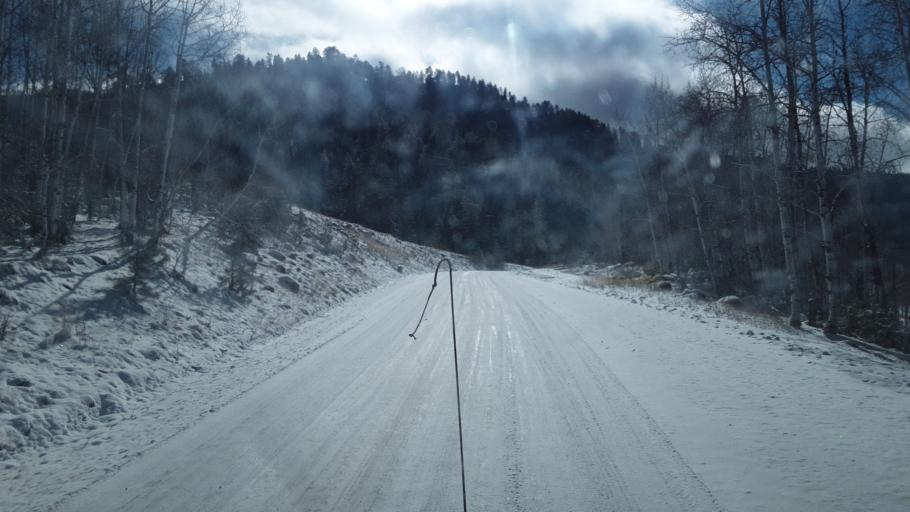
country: US
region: Colorado
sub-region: La Plata County
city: Bayfield
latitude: 37.3961
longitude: -107.6581
